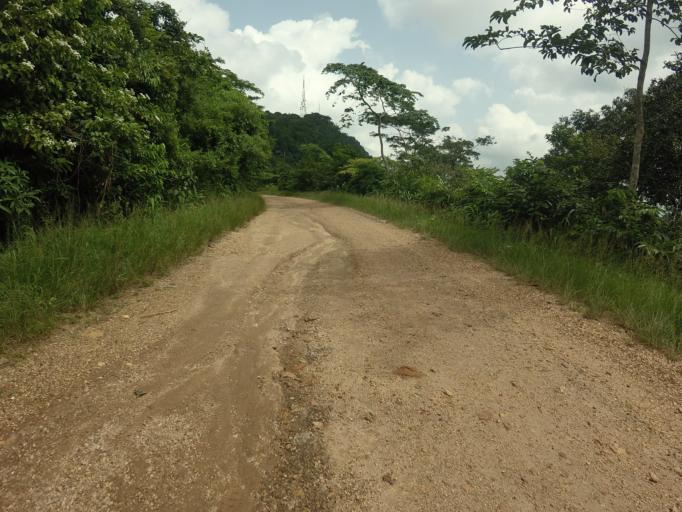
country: GH
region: Volta
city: Kpandu
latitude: 6.8443
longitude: 0.4317
